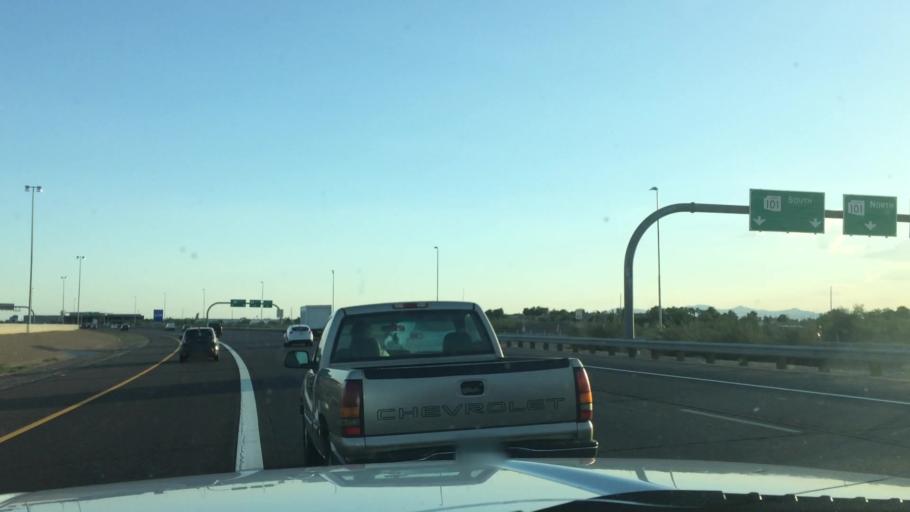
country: US
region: Arizona
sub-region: Maricopa County
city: Sun City
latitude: 33.6647
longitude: -112.2299
